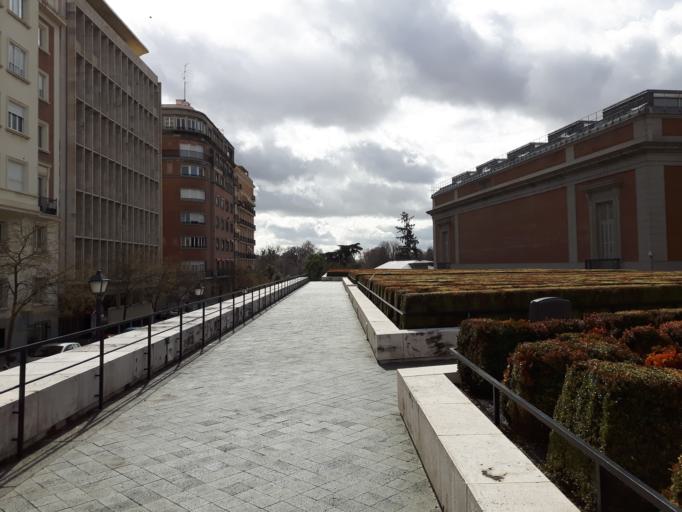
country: ES
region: Madrid
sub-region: Provincia de Madrid
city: Retiro
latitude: 40.4140
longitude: -3.6916
